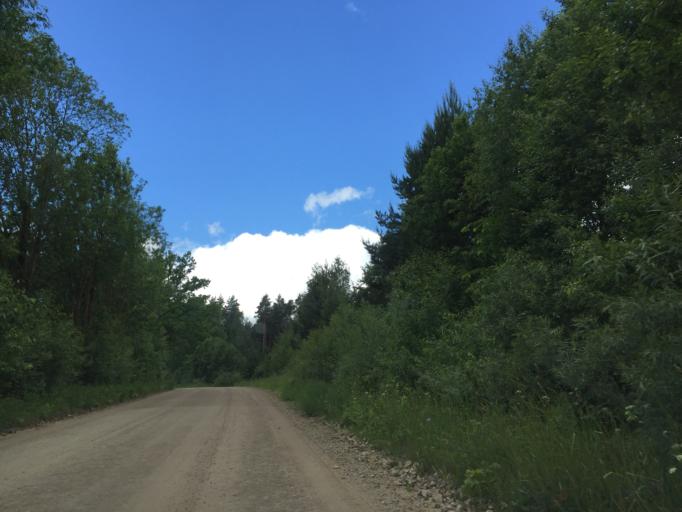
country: LV
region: Lecava
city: Iecava
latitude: 56.6214
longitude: 24.1793
